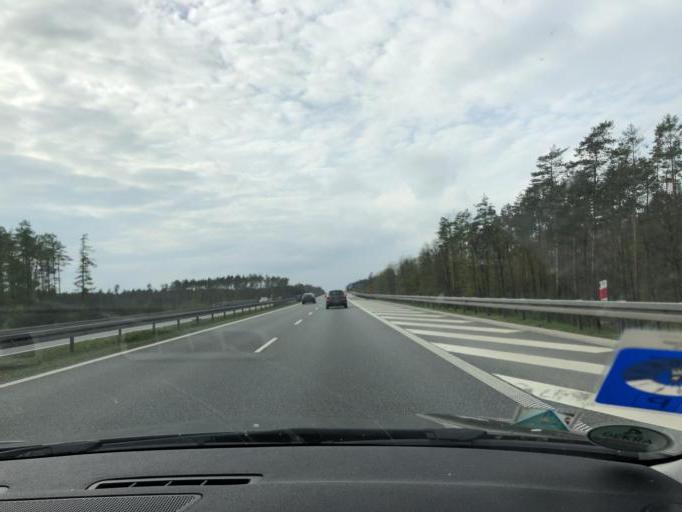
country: PL
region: Opole Voivodeship
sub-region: Powiat opolski
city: Komprachcice
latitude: 50.6137
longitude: 17.7727
